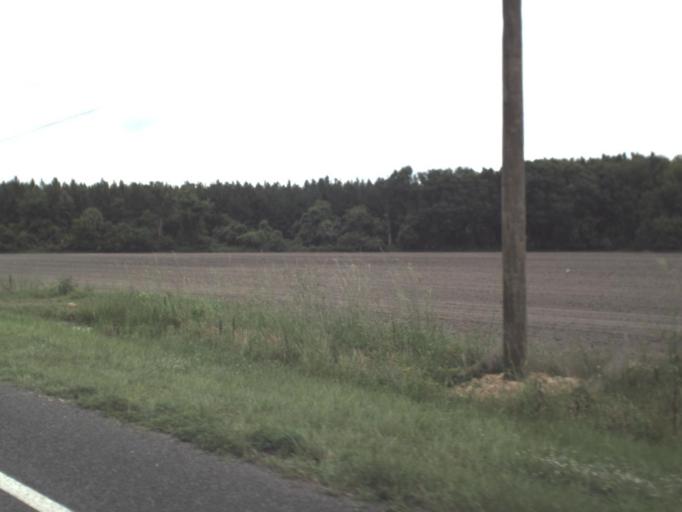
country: US
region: Florida
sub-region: Nassau County
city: Callahan
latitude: 30.6251
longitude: -81.8485
